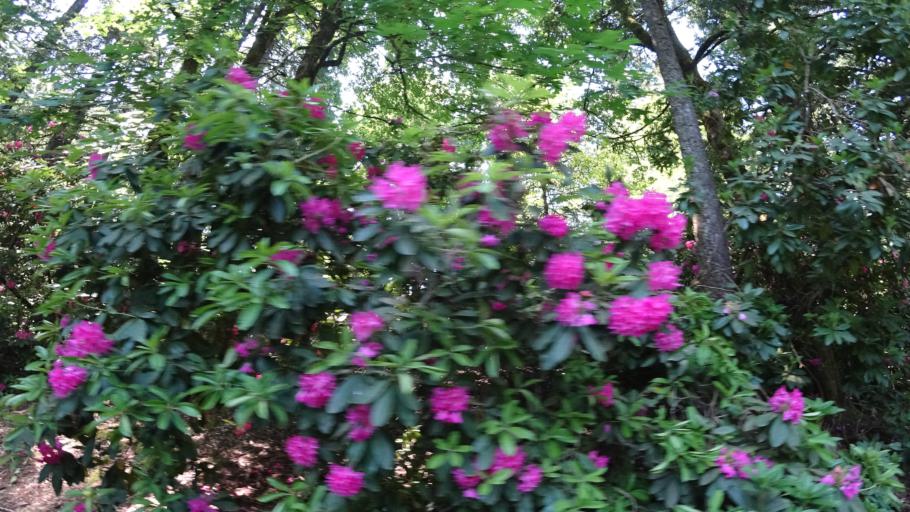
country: US
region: Oregon
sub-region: Clackamas County
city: Lake Oswego
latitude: 45.4320
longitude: -122.7126
